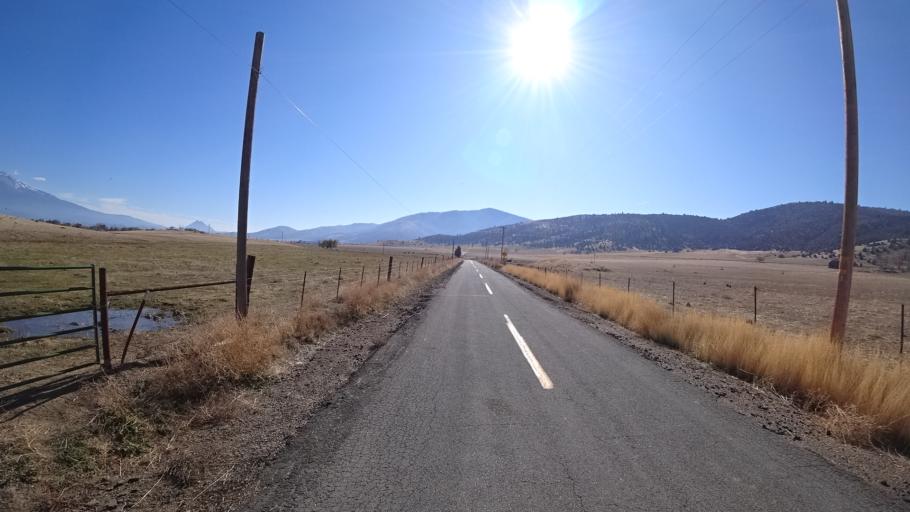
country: US
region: California
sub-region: Siskiyou County
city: Weed
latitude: 41.5306
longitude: -122.5350
